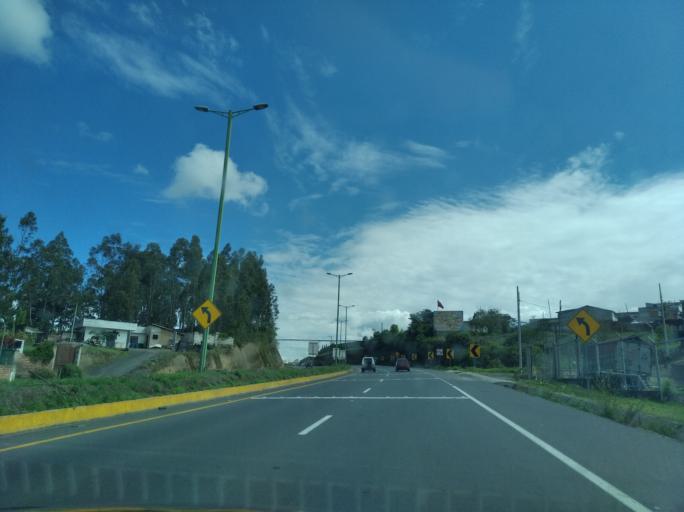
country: EC
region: Pichincha
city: Sangolqui
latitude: -0.1815
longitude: -78.3308
